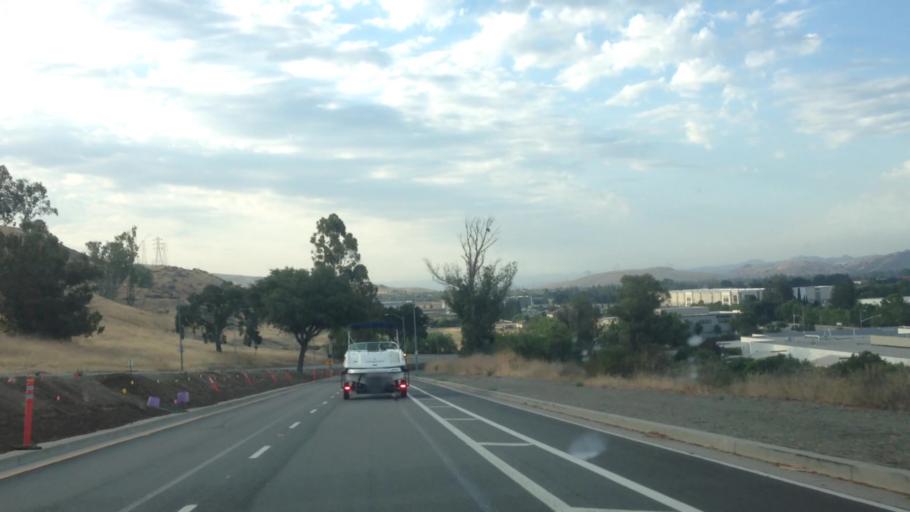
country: US
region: California
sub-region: Santa Clara County
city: Seven Trees
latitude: 37.2636
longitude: -121.7848
